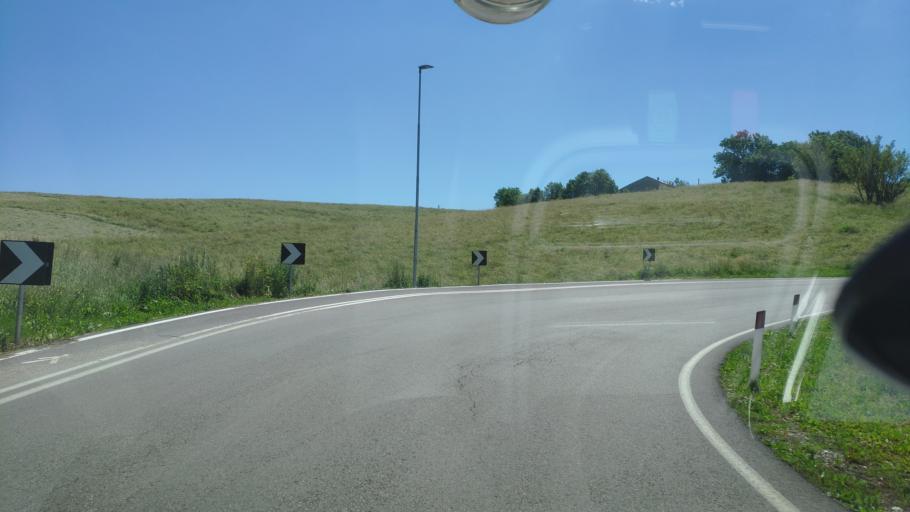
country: IT
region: Veneto
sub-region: Provincia di Vicenza
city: Canove di Roana
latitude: 45.8637
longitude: 11.4784
